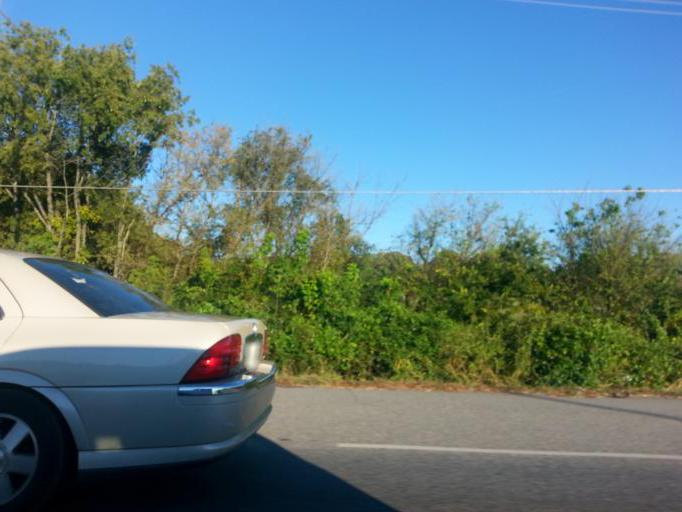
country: US
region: Tennessee
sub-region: Blount County
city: Alcoa
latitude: 35.8038
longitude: -83.9875
